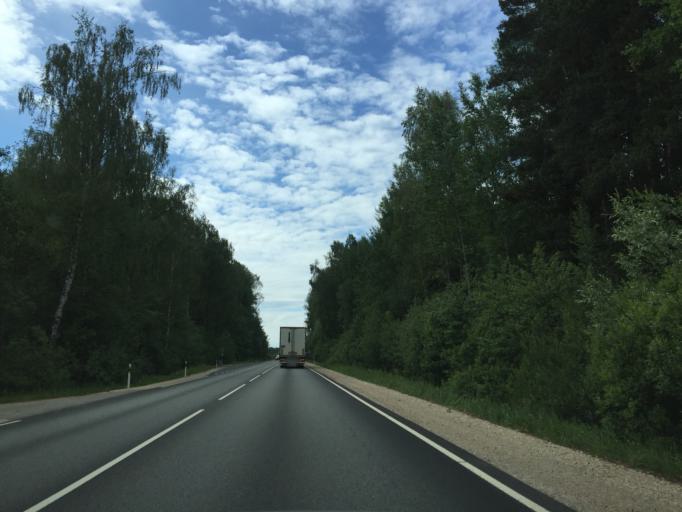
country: LV
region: Ikskile
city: Ikskile
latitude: 56.8800
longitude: 24.5135
